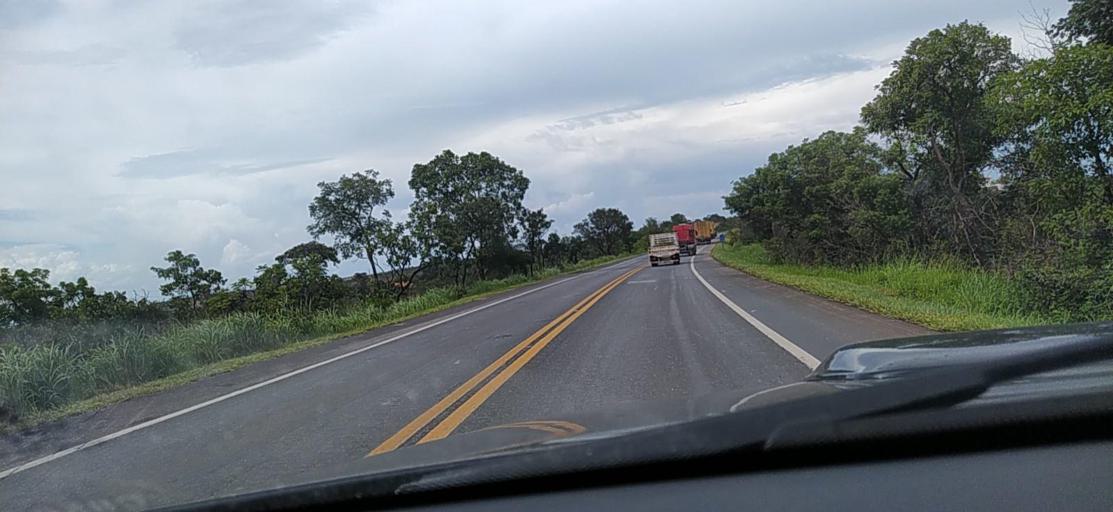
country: BR
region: Minas Gerais
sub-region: Montes Claros
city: Montes Claros
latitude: -16.8469
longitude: -43.8516
